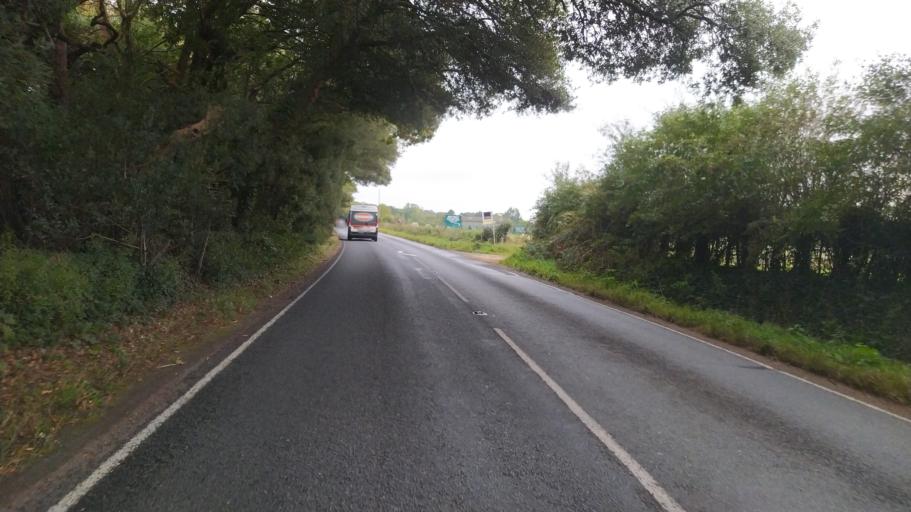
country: GB
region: England
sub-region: Hampshire
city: Brockenhurst
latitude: 50.7883
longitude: -1.5641
